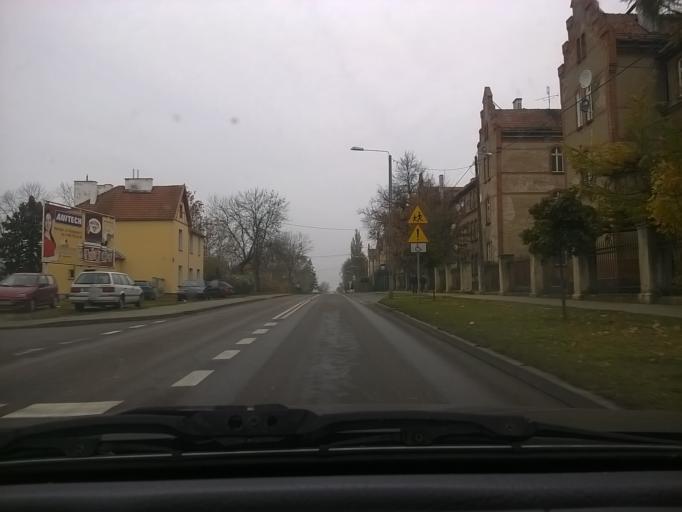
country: PL
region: Warmian-Masurian Voivodeship
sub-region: Powiat ketrzynski
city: Ketrzyn
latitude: 54.0835
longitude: 21.3543
